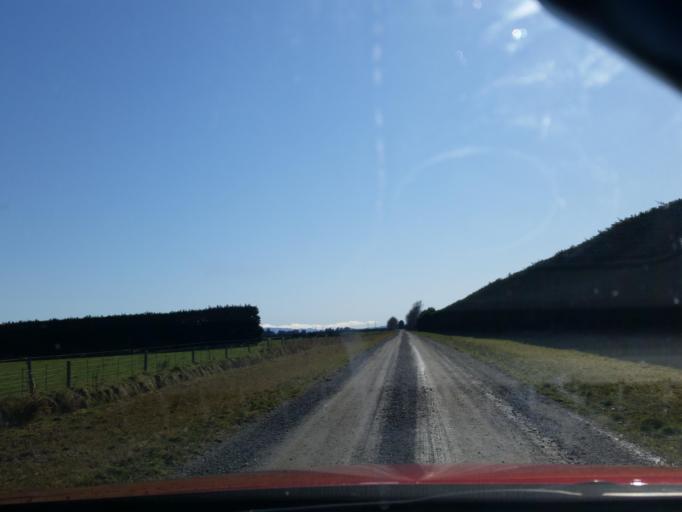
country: NZ
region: Southland
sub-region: Southland District
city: Winton
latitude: -46.1971
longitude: 168.1614
